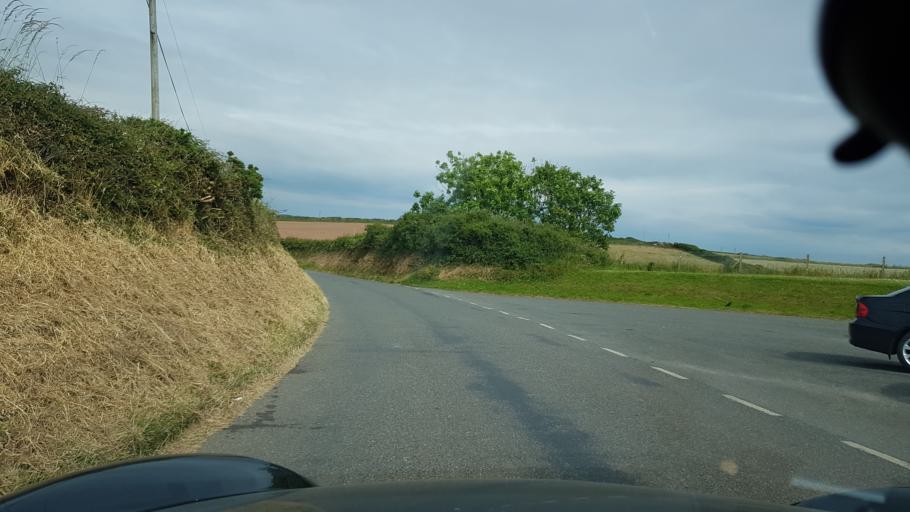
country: GB
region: Wales
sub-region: Pembrokeshire
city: Dale
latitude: 51.7286
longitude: -5.1926
